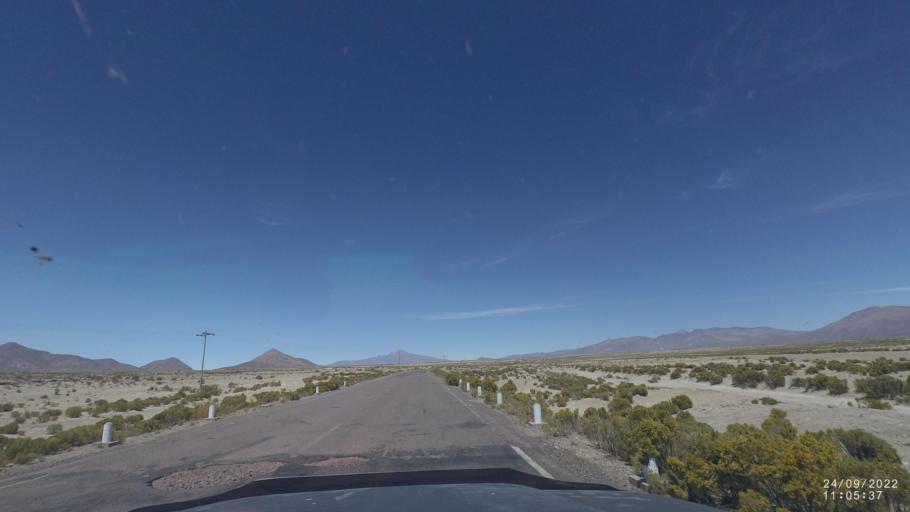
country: BO
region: Oruro
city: Challapata
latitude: -19.4755
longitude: -67.4306
